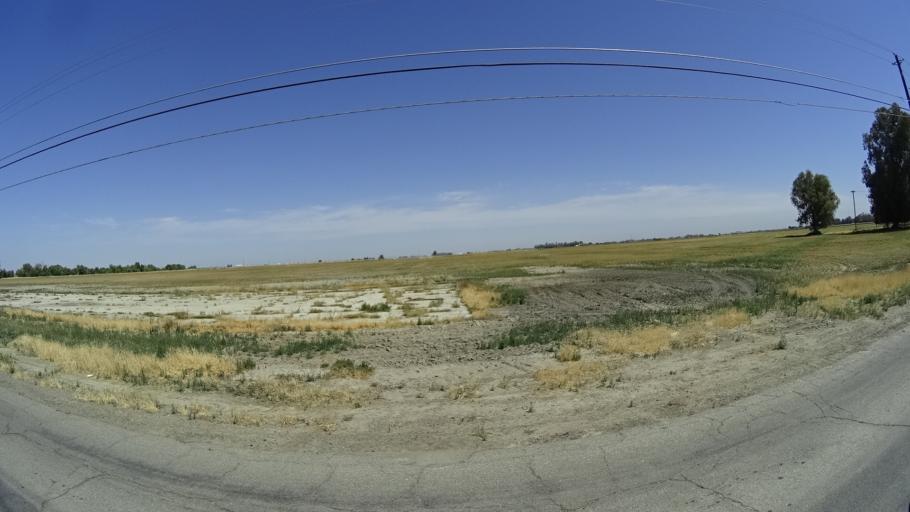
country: US
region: California
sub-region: Kings County
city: Stratford
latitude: 36.1894
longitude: -119.8127
